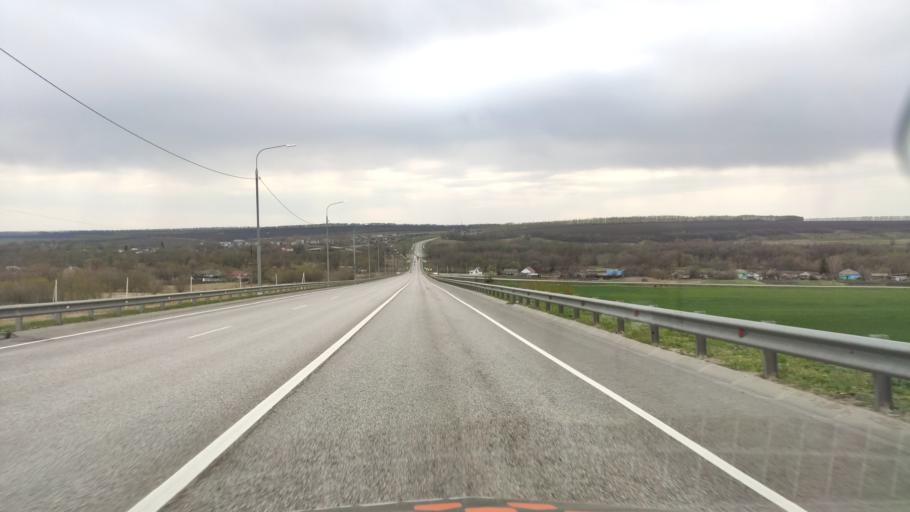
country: RU
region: Voronezj
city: Nizhnedevitsk
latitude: 51.5743
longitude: 38.4809
